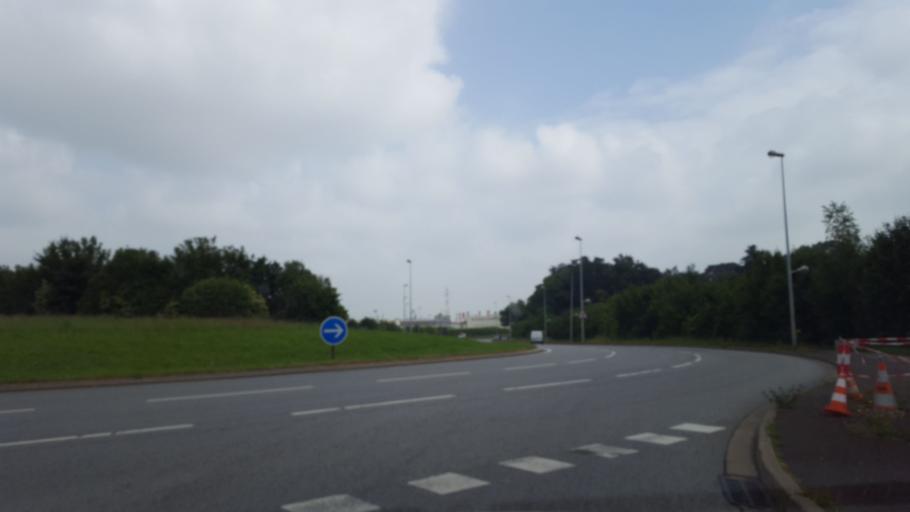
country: FR
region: Brittany
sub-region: Departement d'Ille-et-Vilaine
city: Chartres-de-Bretagne
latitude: 48.0492
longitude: -1.7070
